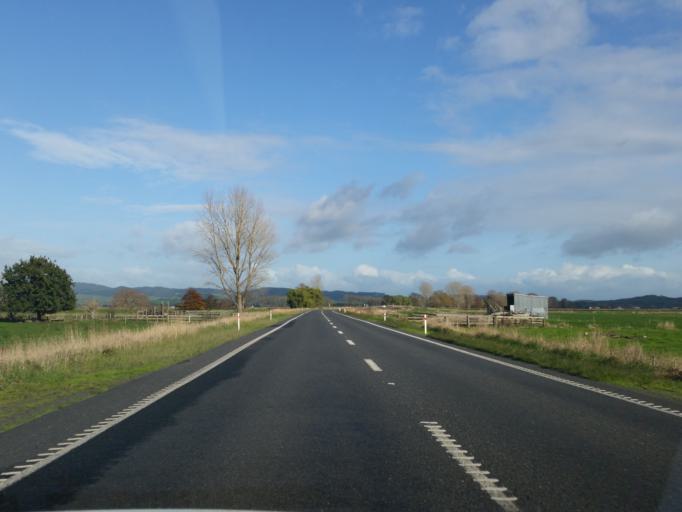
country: NZ
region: Waikato
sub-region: Hauraki District
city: Ngatea
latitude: -37.2770
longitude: 175.4617
